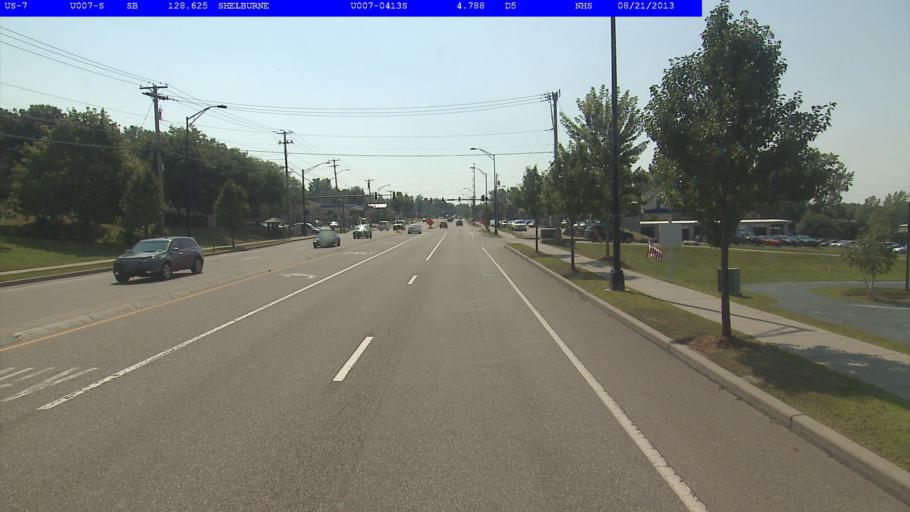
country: US
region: Vermont
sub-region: Chittenden County
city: Burlington
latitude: 44.4233
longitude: -73.2119
